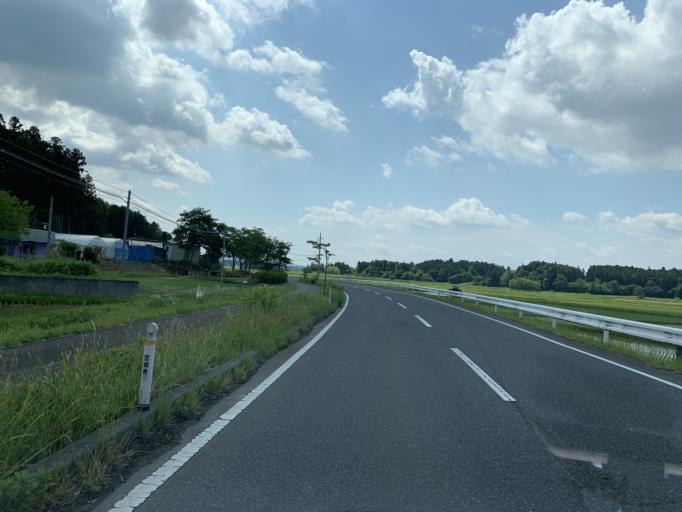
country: JP
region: Miyagi
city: Furukawa
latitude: 38.6740
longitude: 140.9850
